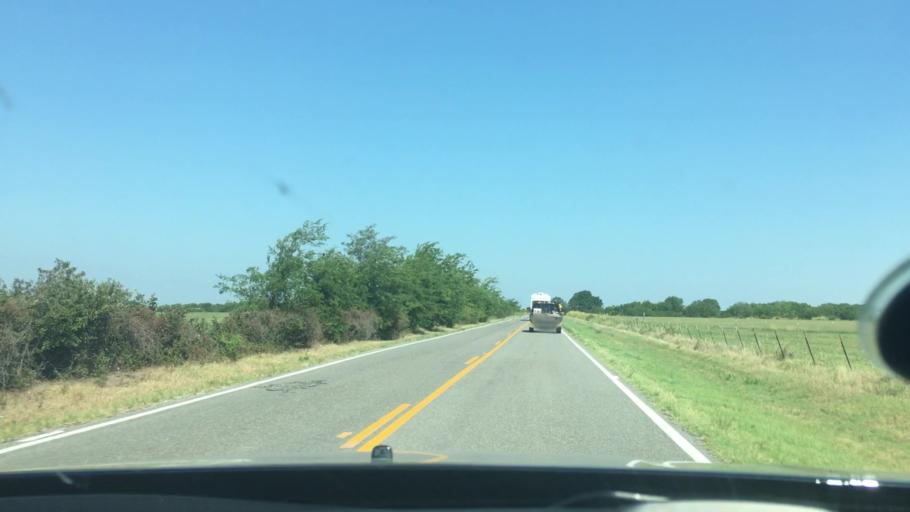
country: US
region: Oklahoma
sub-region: Johnston County
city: Tishomingo
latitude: 34.1968
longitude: -96.5395
